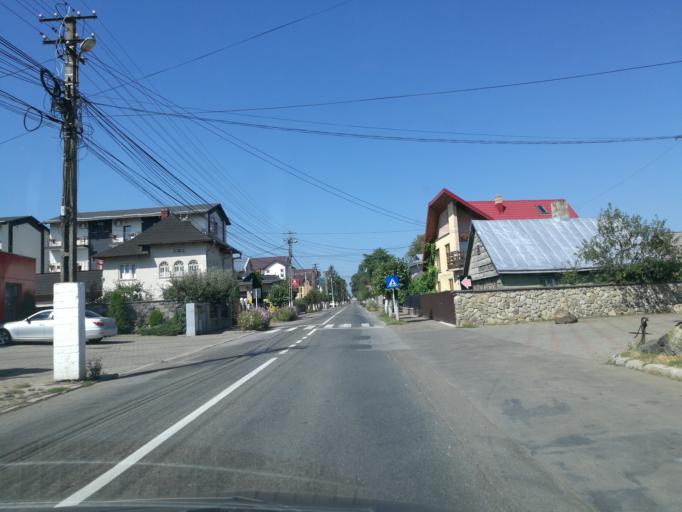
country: RO
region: Suceava
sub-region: Municipiul Suceava
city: Radauti
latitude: 47.8525
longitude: 25.8974
